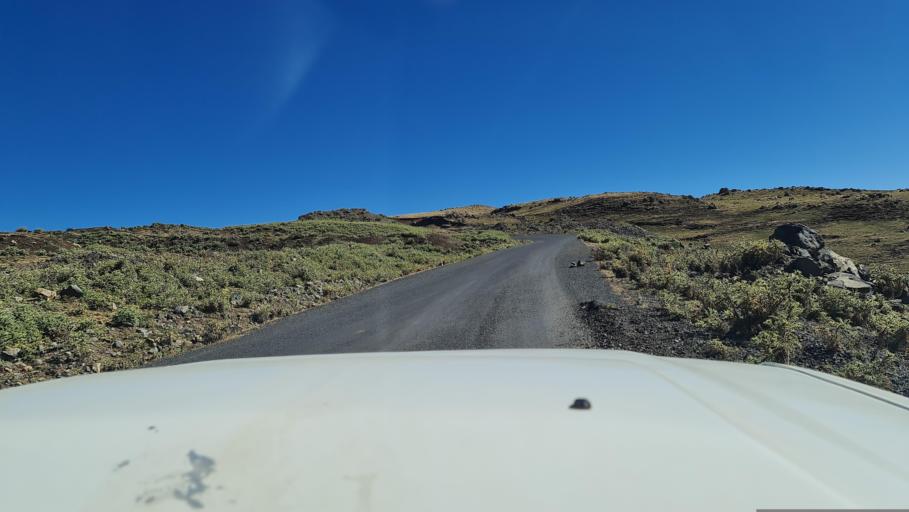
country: ET
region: Amhara
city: Debark'
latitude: 13.1352
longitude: 38.1767
